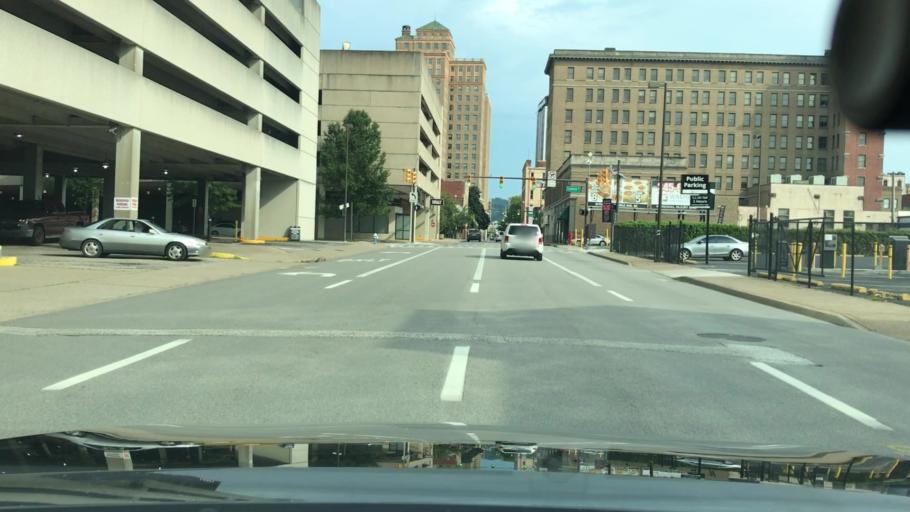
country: US
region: West Virginia
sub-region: Kanawha County
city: Charleston
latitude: 38.3529
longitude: -81.6351
